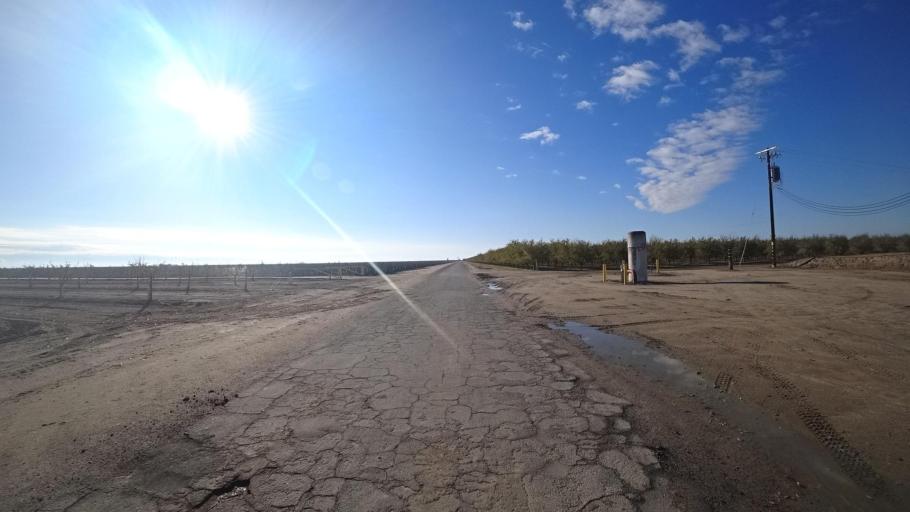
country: US
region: California
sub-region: Kern County
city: McFarland
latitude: 35.7110
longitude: -119.2941
